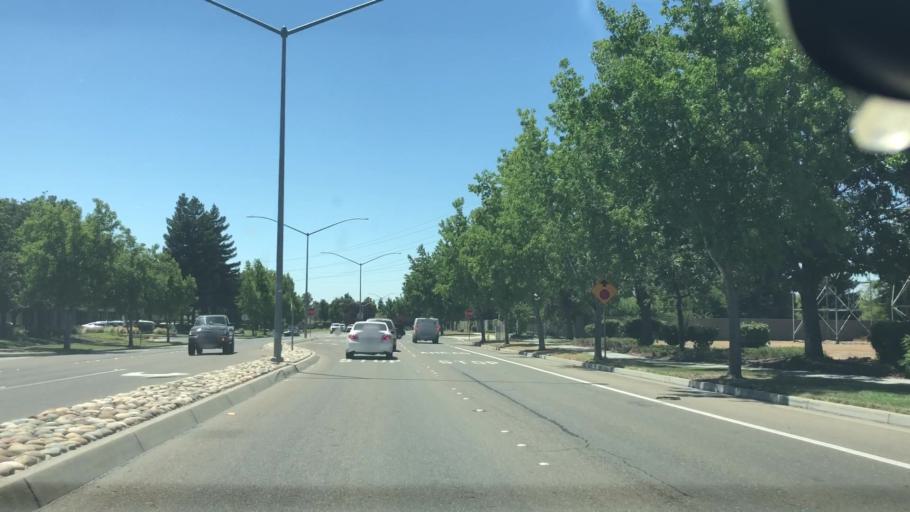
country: US
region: California
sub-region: San Joaquin County
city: Tracy
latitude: 37.7252
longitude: -121.4354
